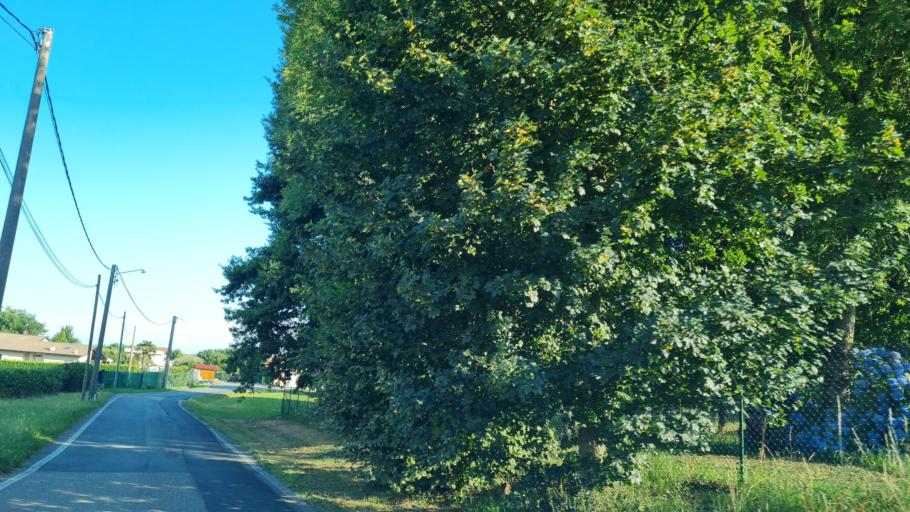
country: IT
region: Piedmont
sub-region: Provincia di Biella
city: Occhieppo Superiore
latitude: 45.5540
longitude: 8.0088
